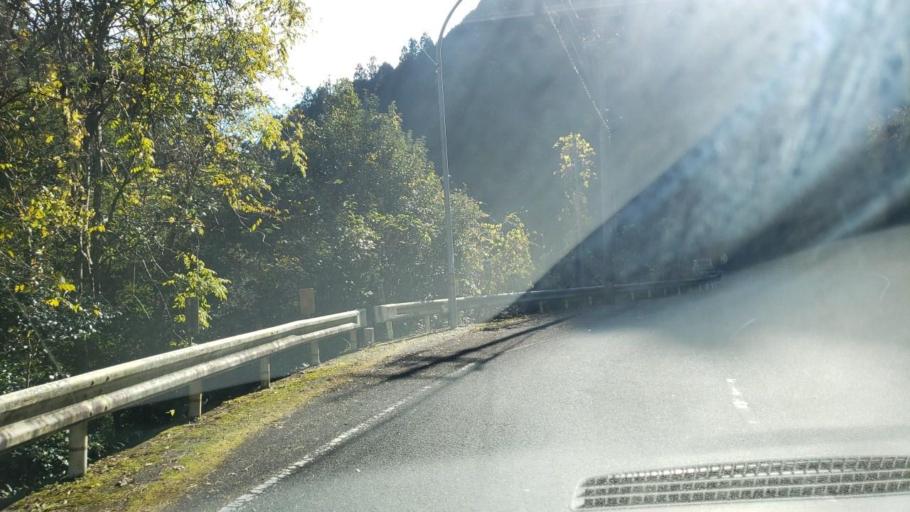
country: JP
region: Tokushima
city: Wakimachi
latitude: 34.0070
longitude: 134.0339
